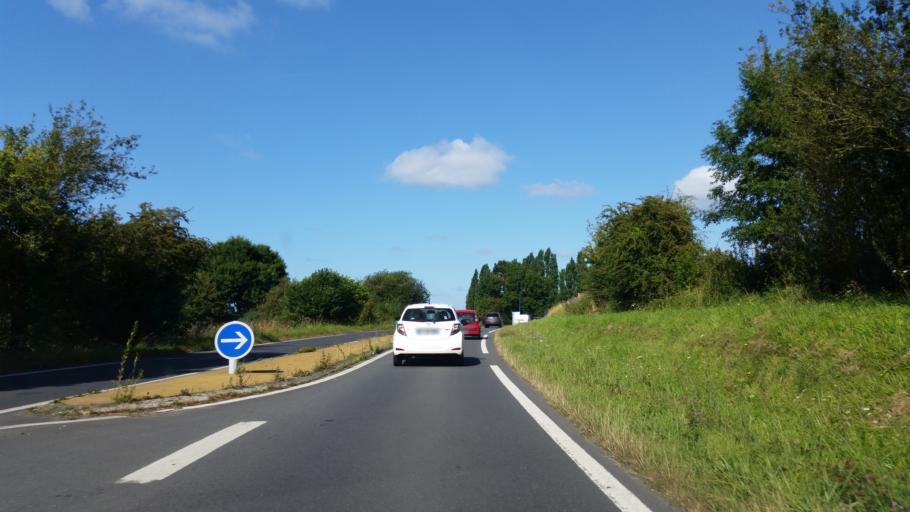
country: FR
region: Lower Normandy
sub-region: Departement du Calvados
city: Amfreville
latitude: 49.2606
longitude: -0.2360
